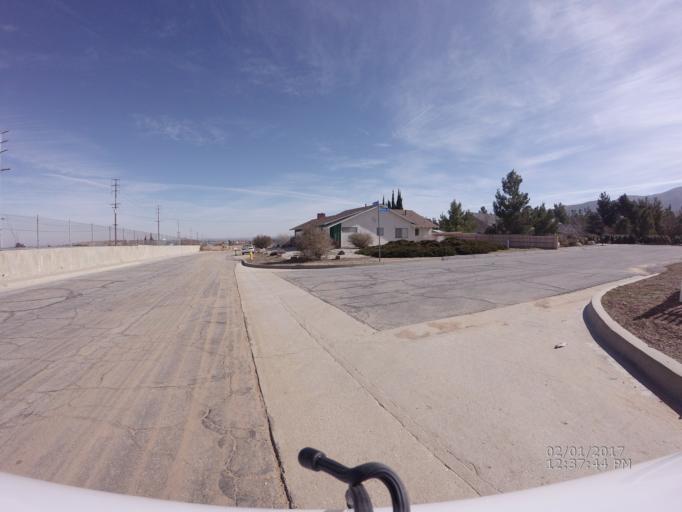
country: US
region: California
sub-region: Los Angeles County
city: Desert View Highlands
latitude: 34.5577
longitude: -118.1489
